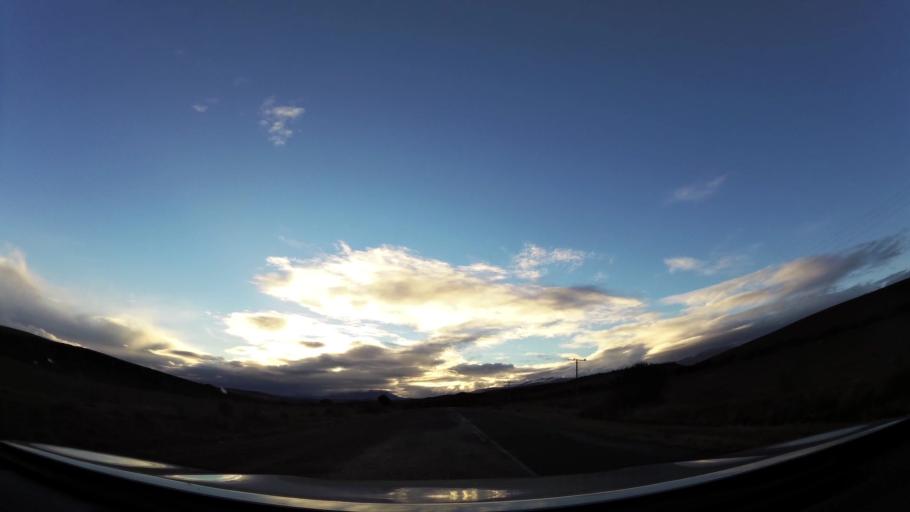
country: ZA
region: Western Cape
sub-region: Eden District Municipality
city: Riversdale
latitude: -34.0710
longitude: 20.9037
